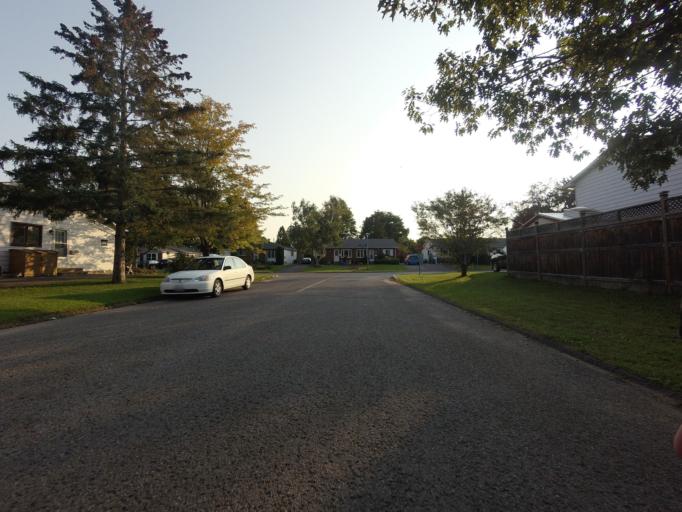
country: CA
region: Ontario
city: Bells Corners
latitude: 45.2883
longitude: -75.8779
